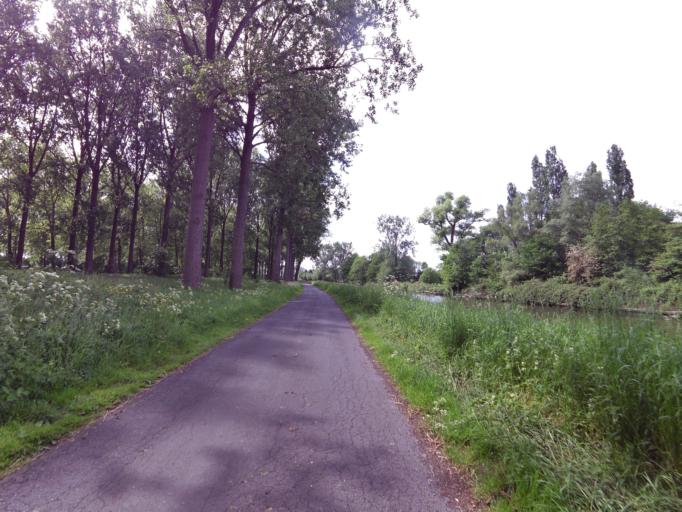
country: BE
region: Flanders
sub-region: Provincie West-Vlaanderen
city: Oostkamp
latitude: 51.1717
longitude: 3.2455
